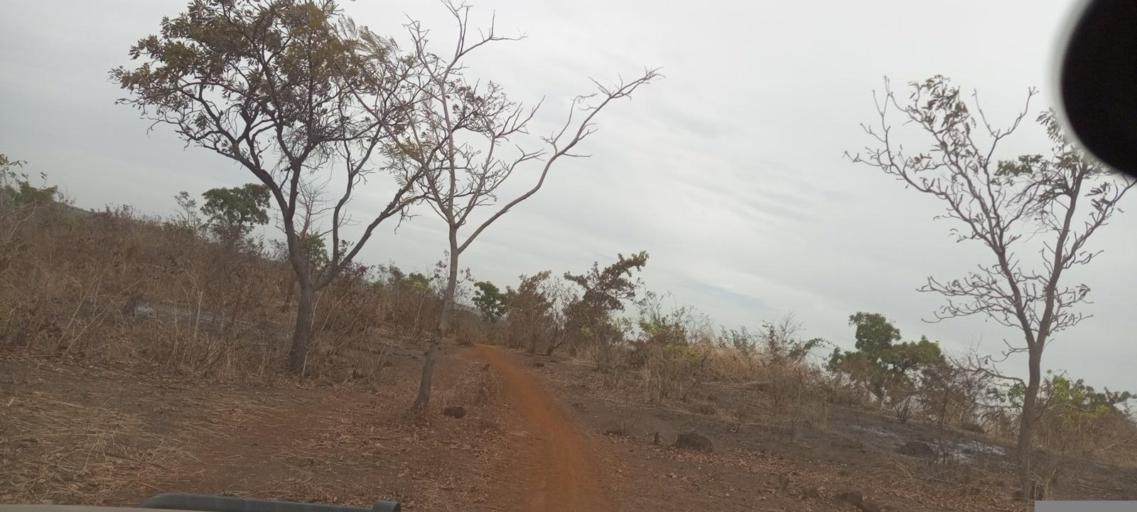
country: ML
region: Koulikoro
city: Kati
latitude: 12.8267
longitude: -8.4580
